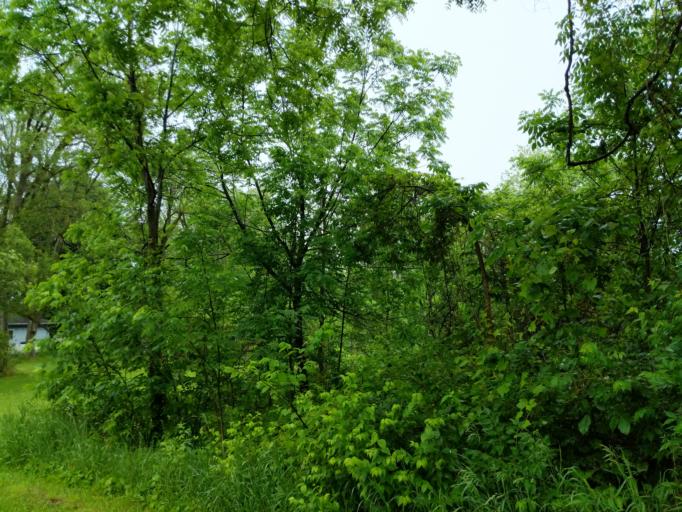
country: US
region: Michigan
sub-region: Berrien County
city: Coloma
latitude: 42.1745
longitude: -86.3079
